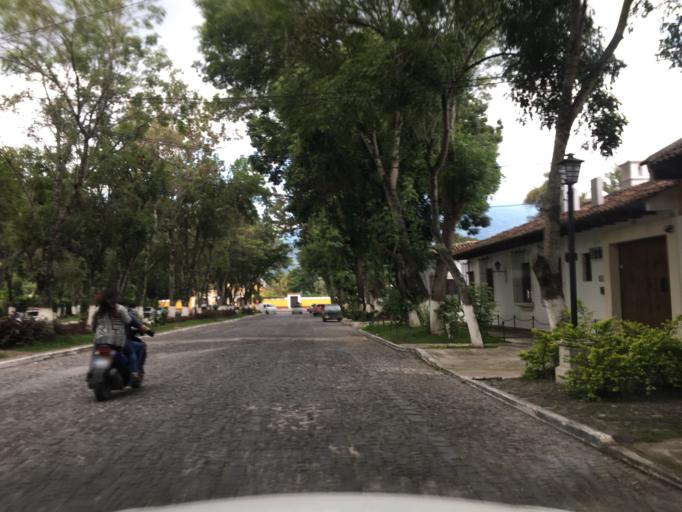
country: GT
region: Sacatepequez
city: Antigua Guatemala
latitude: 14.5468
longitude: -90.7301
